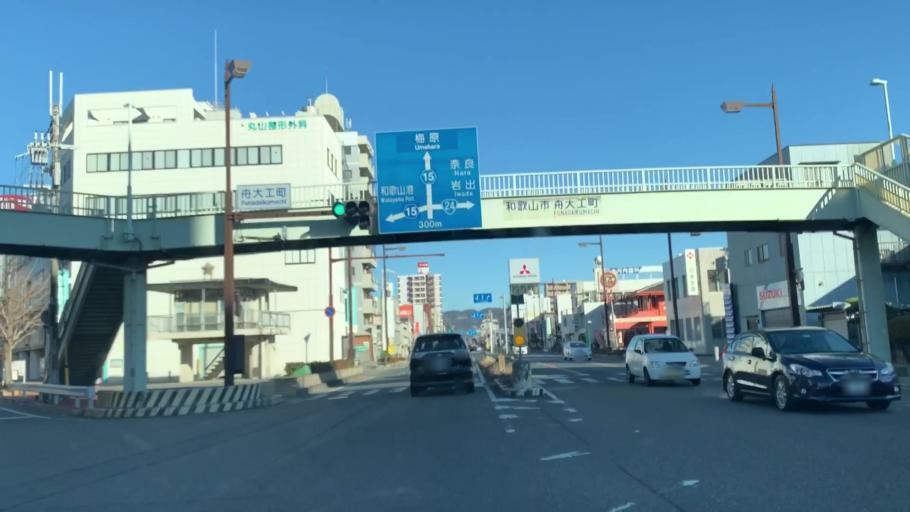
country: JP
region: Wakayama
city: Wakayama-shi
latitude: 34.2339
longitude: 135.1695
